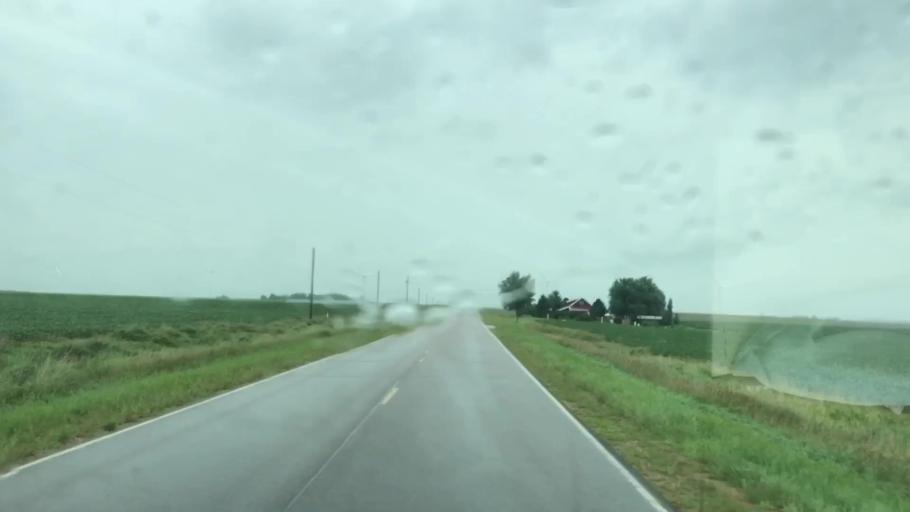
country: US
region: Iowa
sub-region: O'Brien County
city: Sanborn
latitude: 43.2135
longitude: -95.7234
